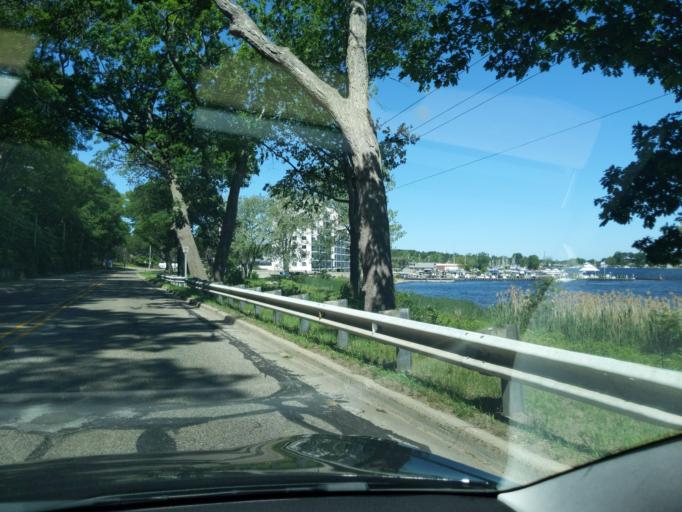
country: US
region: Michigan
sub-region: Muskegon County
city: Roosevelt Park
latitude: 43.2145
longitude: -86.3130
